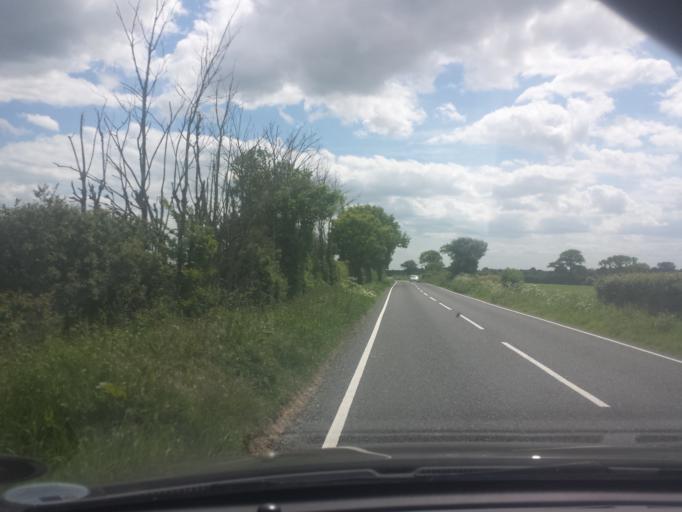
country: GB
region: England
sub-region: Essex
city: Little Clacton
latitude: 51.8355
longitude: 1.1556
